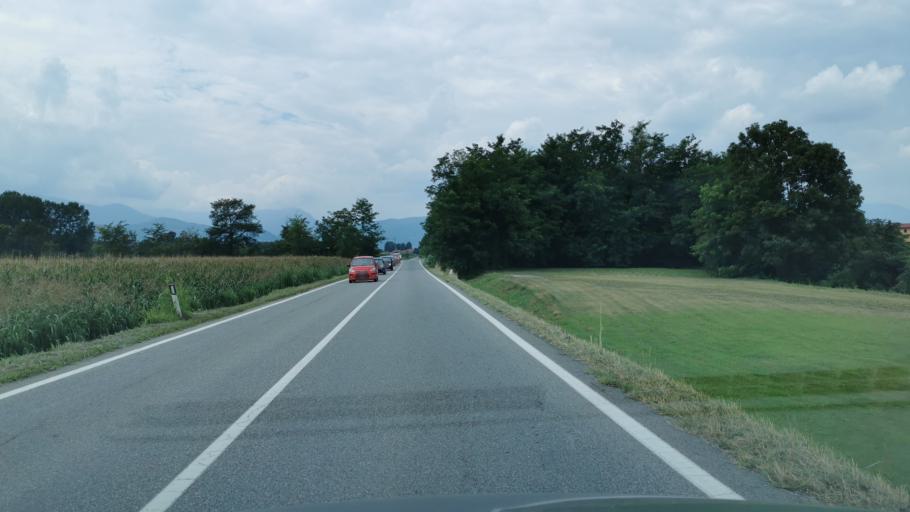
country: IT
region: Piedmont
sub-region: Provincia di Torino
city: Garzigliana
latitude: 44.8346
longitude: 7.3618
